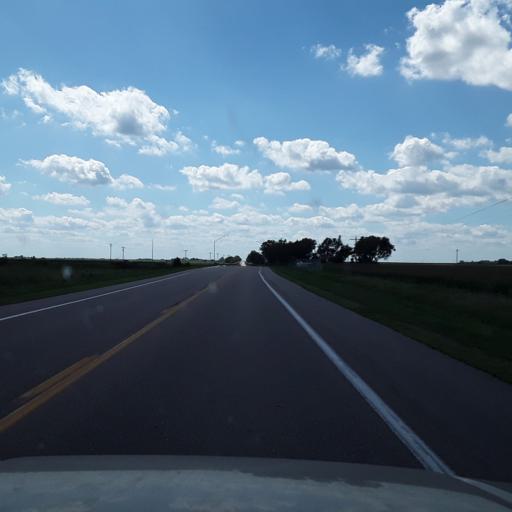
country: US
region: Nebraska
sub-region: Merrick County
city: Central City
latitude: 41.1911
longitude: -97.9981
